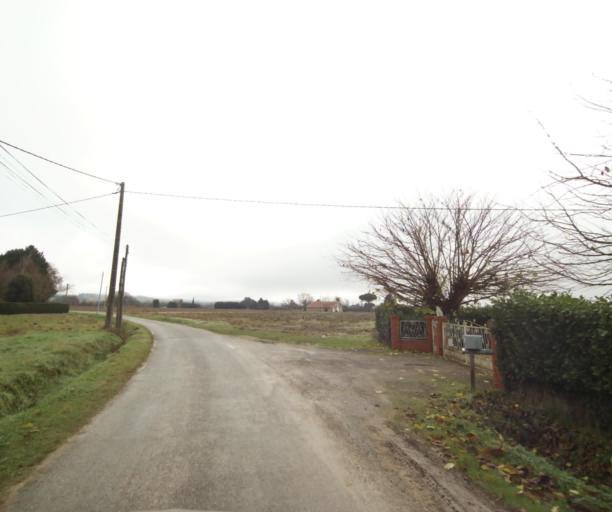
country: FR
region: Midi-Pyrenees
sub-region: Departement de la Haute-Garonne
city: Villemur-sur-Tarn
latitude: 43.8741
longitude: 1.4758
